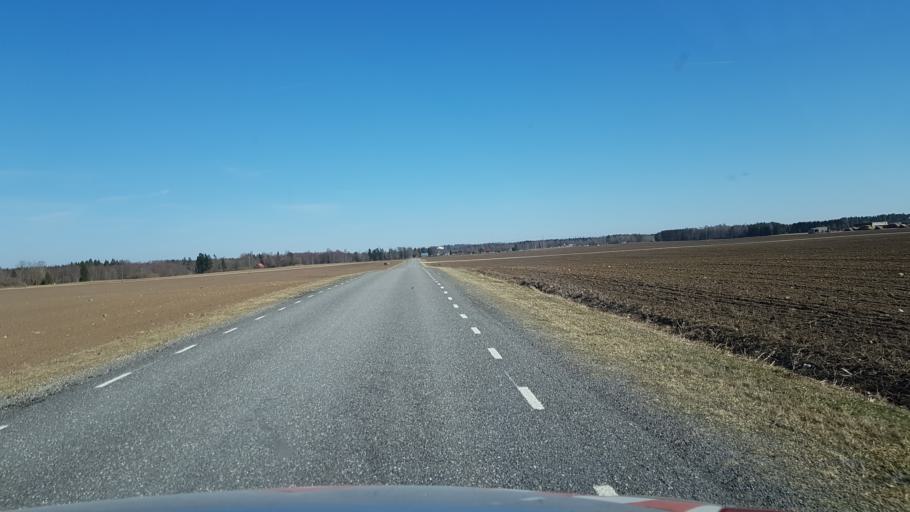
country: EE
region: Laeaene-Virumaa
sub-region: Rakke vald
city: Rakke
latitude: 59.0061
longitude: 26.1808
